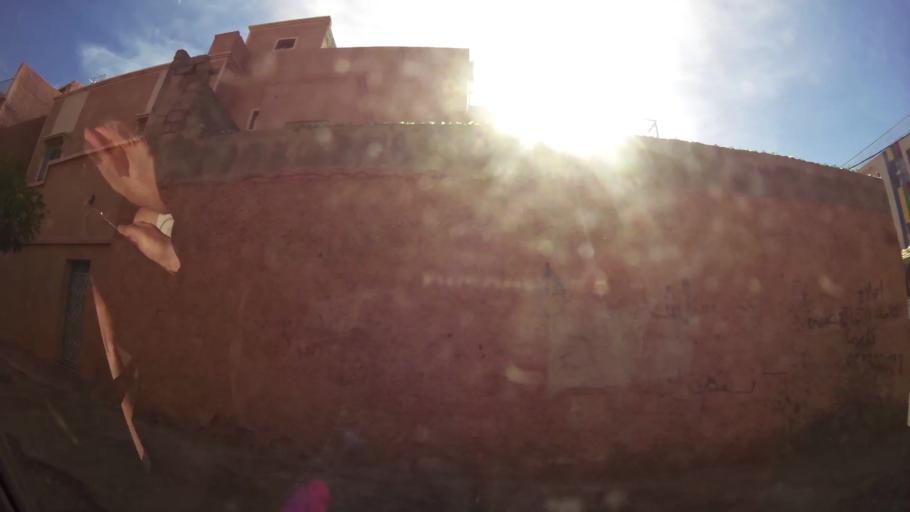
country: MA
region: Marrakech-Tensift-Al Haouz
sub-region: Marrakech
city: Marrakesh
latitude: 31.6460
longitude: -8.0055
